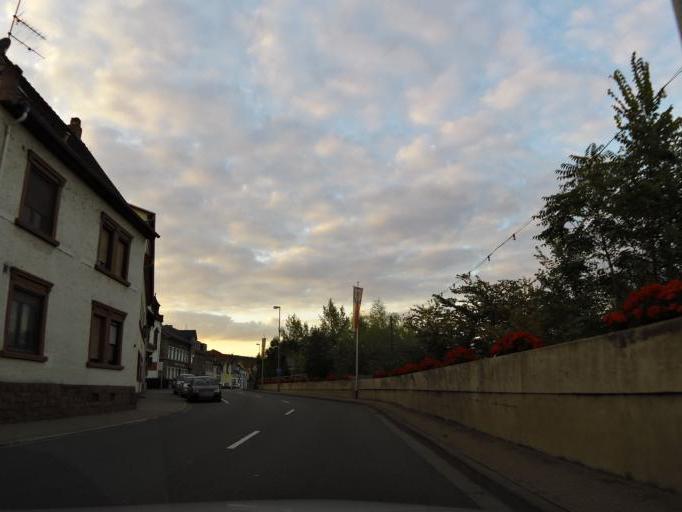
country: DE
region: Rheinland-Pfalz
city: Nierstein
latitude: 49.8770
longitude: 8.3414
